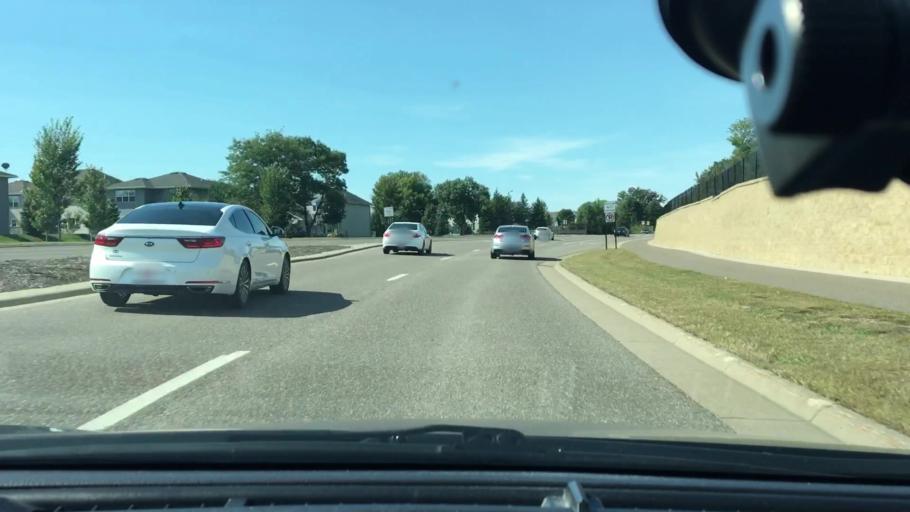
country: US
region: Minnesota
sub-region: Hennepin County
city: Corcoran
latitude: 45.0823
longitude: -93.5051
